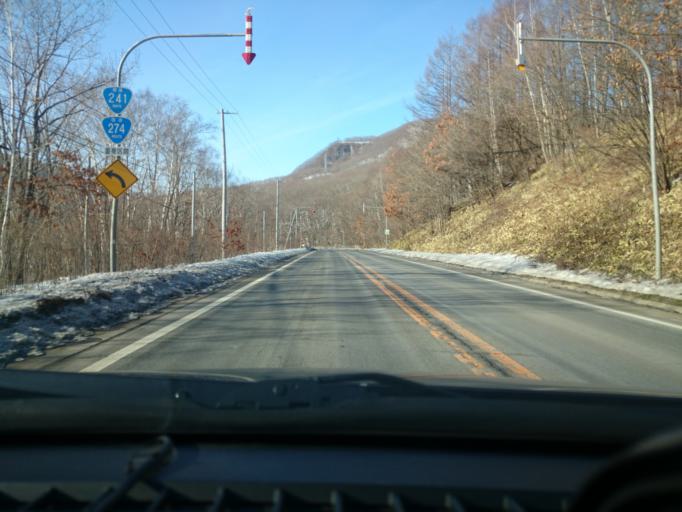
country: JP
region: Hokkaido
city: Otofuke
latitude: 43.2530
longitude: 143.4724
